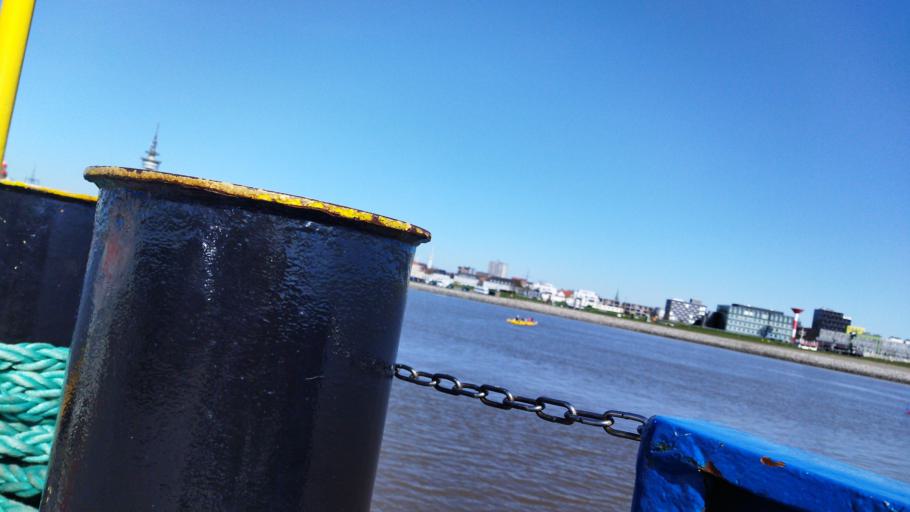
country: DE
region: Bremen
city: Bremerhaven
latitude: 53.5339
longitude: 8.5721
